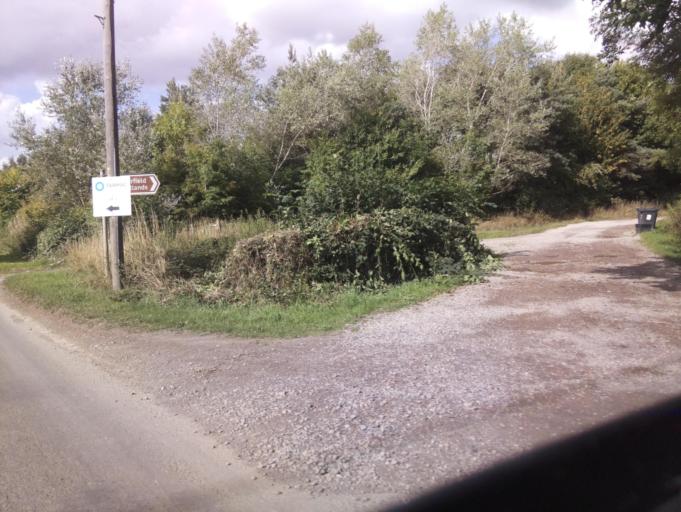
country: GB
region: England
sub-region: North Yorkshire
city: Bedale
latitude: 54.2355
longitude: -1.6740
